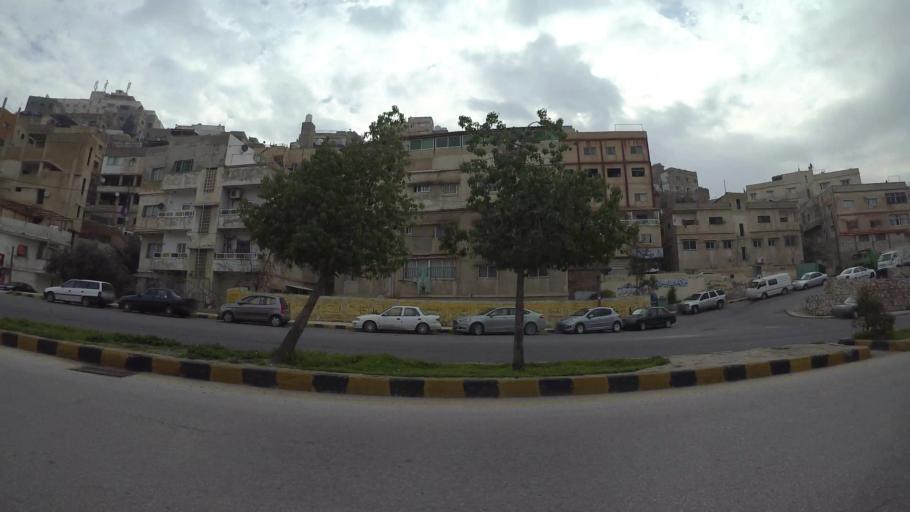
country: JO
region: Amman
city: Amman
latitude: 31.9637
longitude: 35.9345
